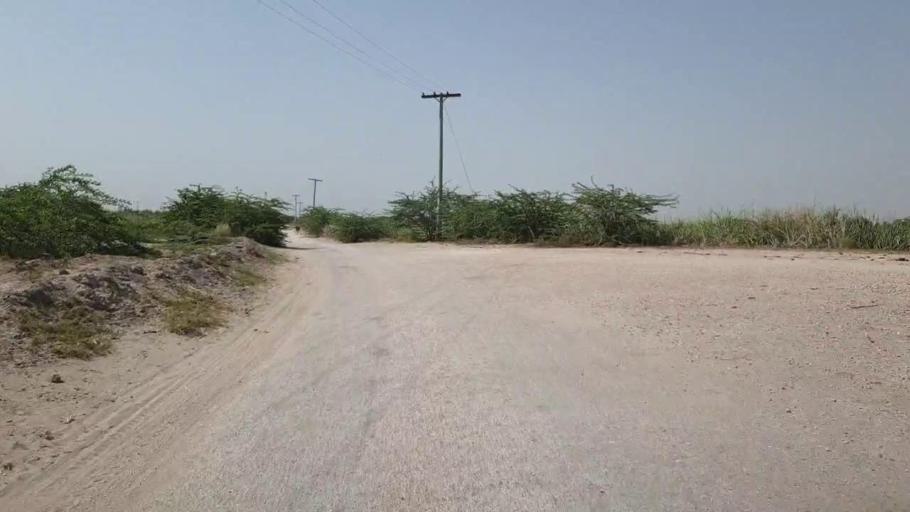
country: PK
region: Sindh
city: Jam Sahib
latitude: 26.4315
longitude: 68.9153
